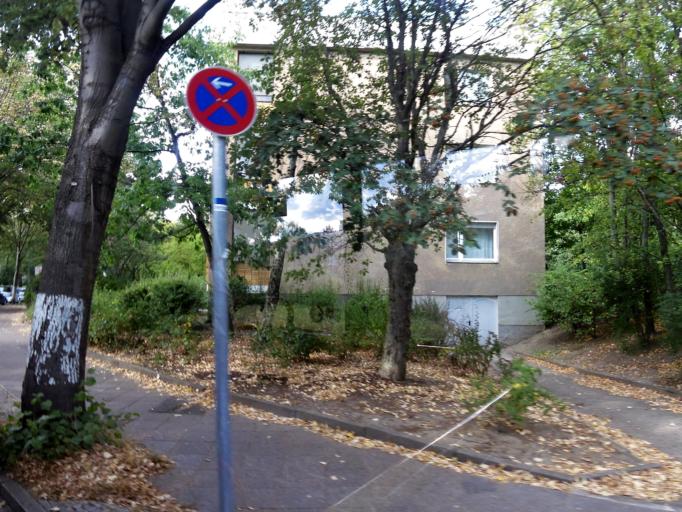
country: DE
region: Berlin
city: Marienfelde
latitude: 52.4292
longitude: 13.3593
